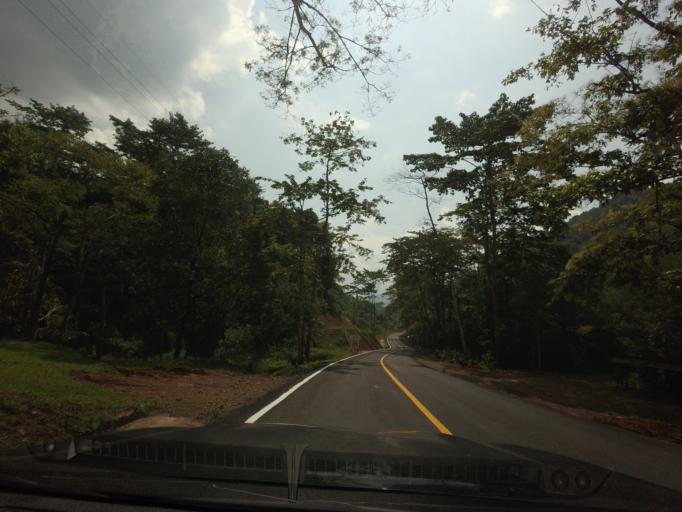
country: TH
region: Nan
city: Bo Kluea
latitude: 19.1782
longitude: 101.1723
